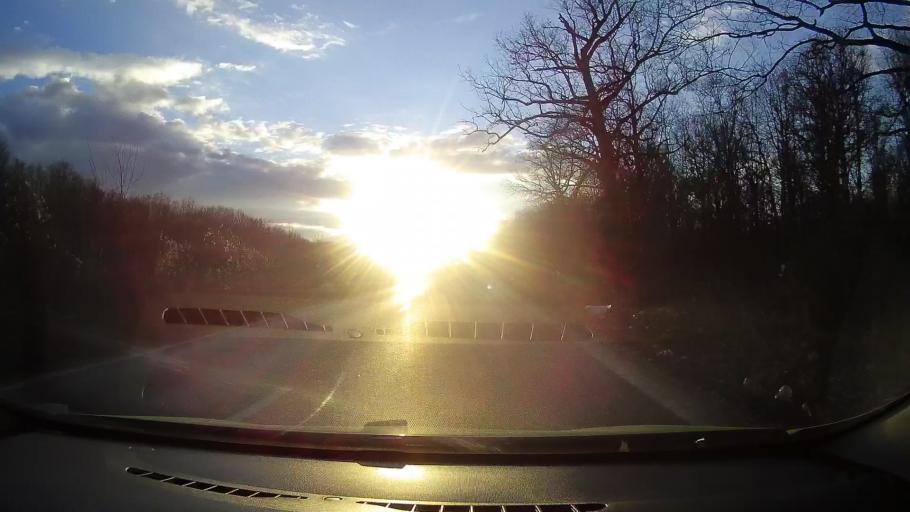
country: RO
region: Dambovita
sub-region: Comuna I. L. Caragiale
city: Mija
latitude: 44.9133
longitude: 25.6442
